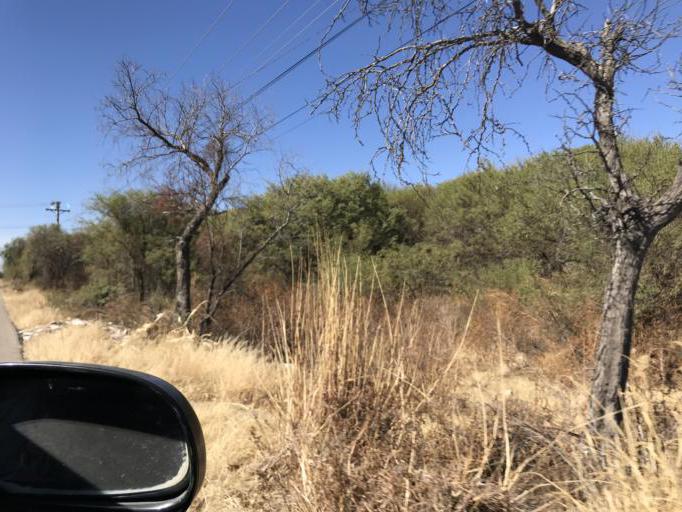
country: BO
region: Cochabamba
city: Tarata
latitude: -17.5727
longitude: -66.0660
